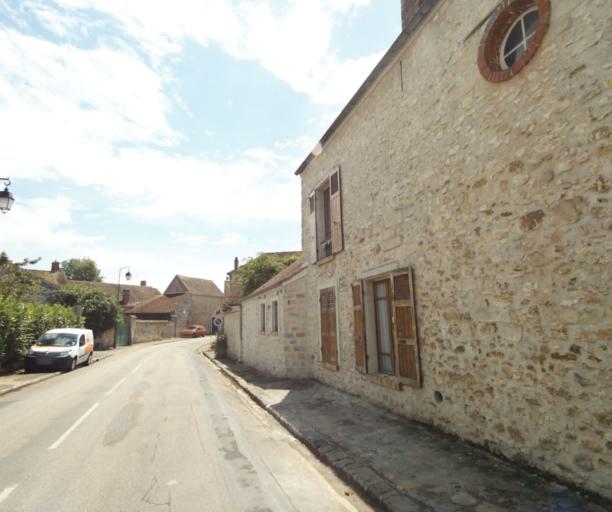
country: FR
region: Ile-de-France
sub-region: Departement de Seine-et-Marne
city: Cely
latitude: 48.4586
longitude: 2.5372
